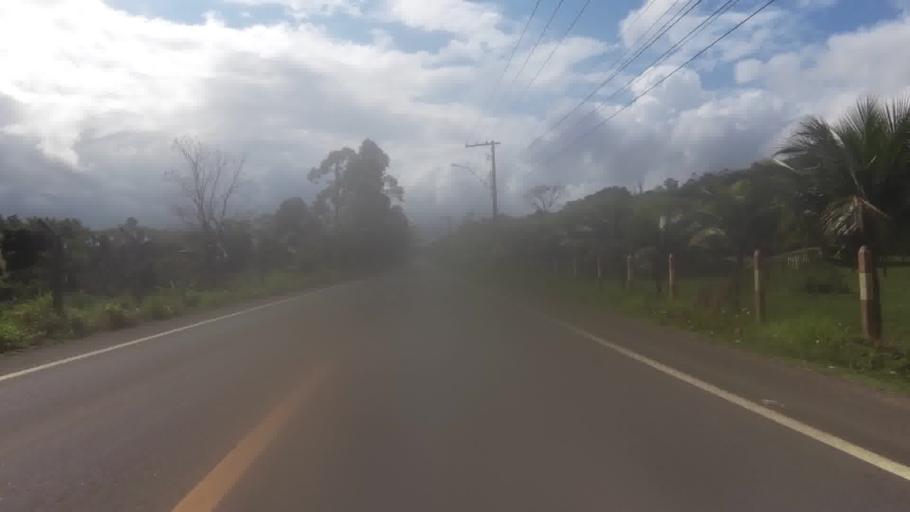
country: BR
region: Espirito Santo
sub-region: Piuma
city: Piuma
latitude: -20.8125
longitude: -40.6845
